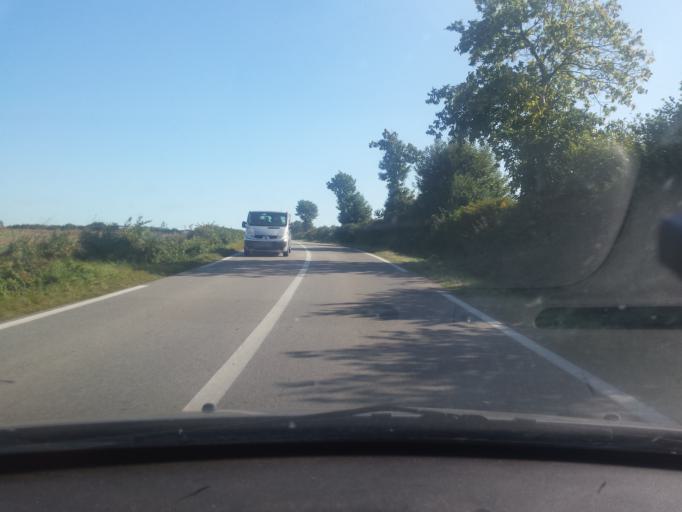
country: FR
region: Brittany
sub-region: Departement du Morbihan
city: Saint-Thuriau
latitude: 48.0318
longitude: -2.9193
